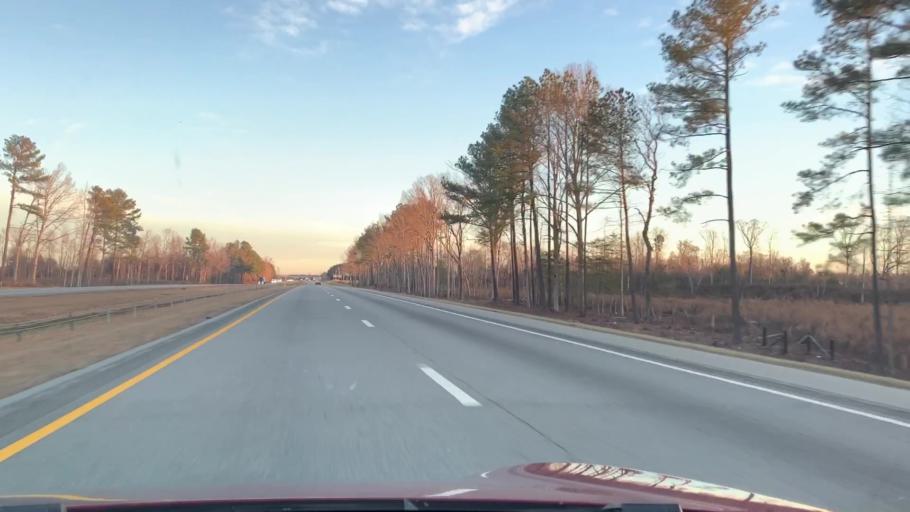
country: US
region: North Carolina
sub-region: Halifax County
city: Enfield
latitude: 36.2030
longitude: -77.7579
